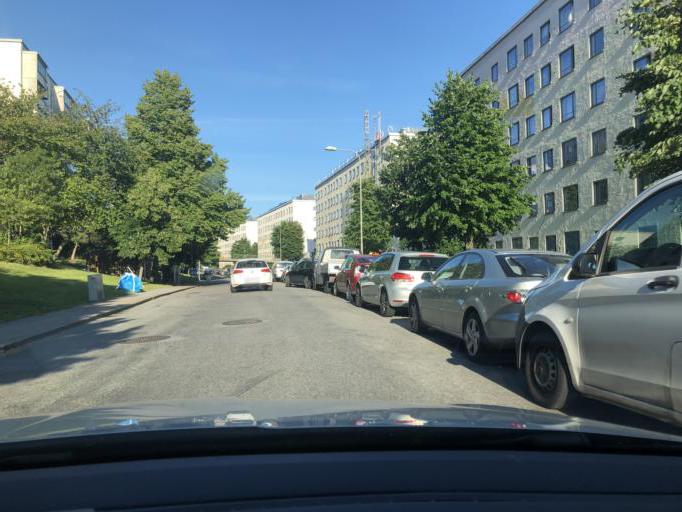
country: SE
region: Stockholm
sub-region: Huddinge Kommun
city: Segeltorp
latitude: 59.2774
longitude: 17.9038
